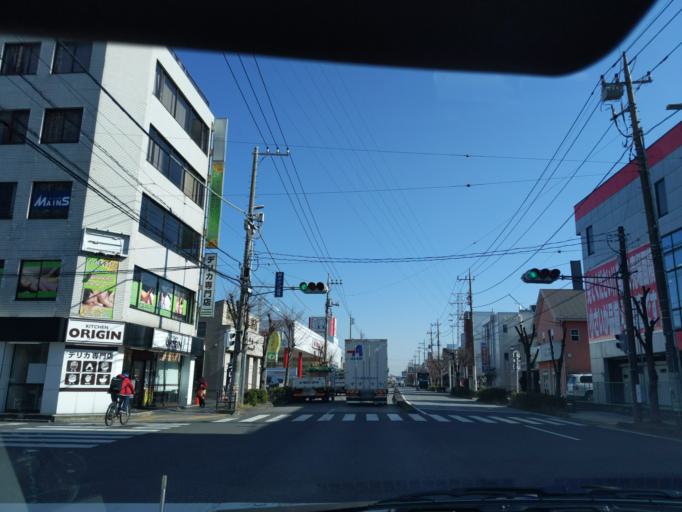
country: JP
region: Saitama
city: Yashio-shi
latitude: 35.8208
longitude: 139.8363
